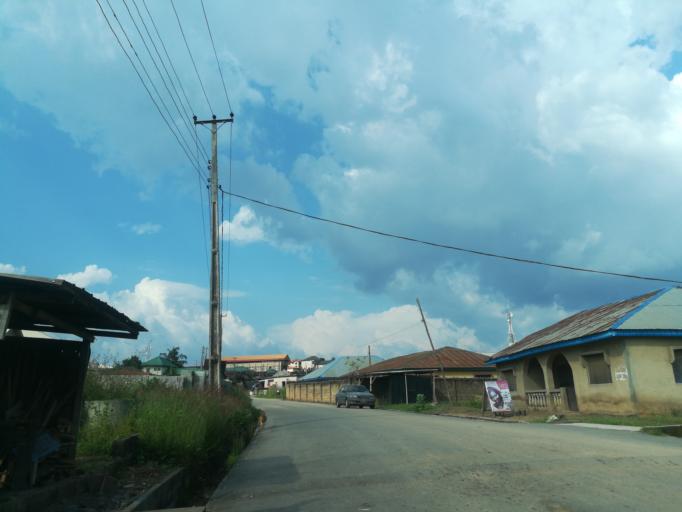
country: NG
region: Oyo
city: Ibadan
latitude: 7.4186
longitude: 3.8425
